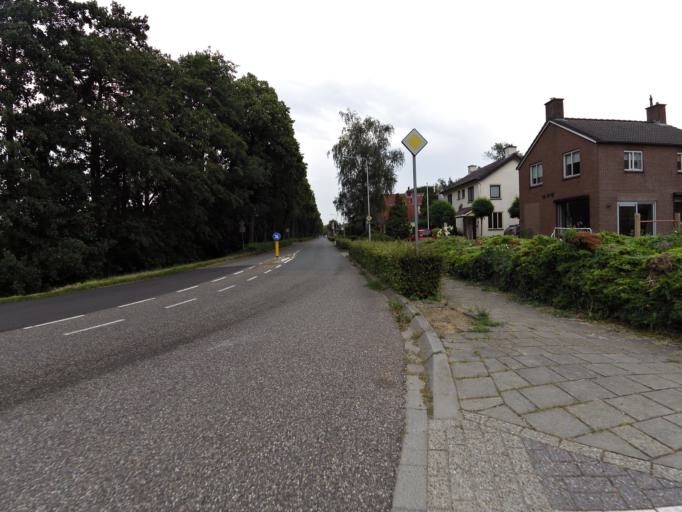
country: NL
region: Gelderland
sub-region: Gemeente Groesbeek
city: Berg en Dal
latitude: 51.8745
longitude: 5.9573
